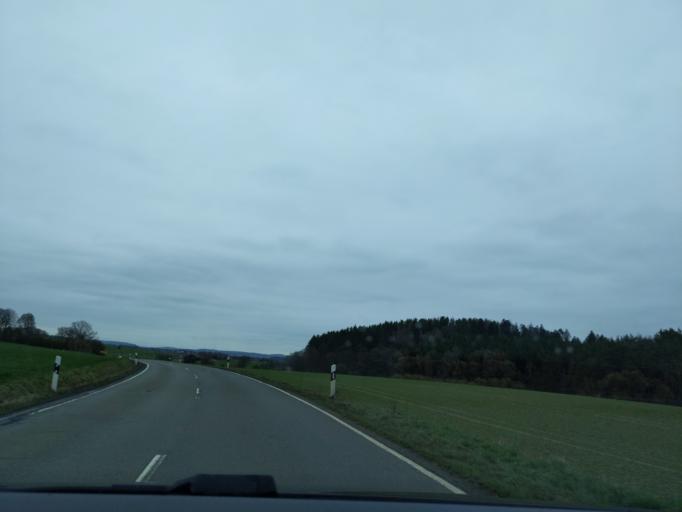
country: DE
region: Hesse
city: Frankenberg
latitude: 51.0330
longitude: 8.8215
